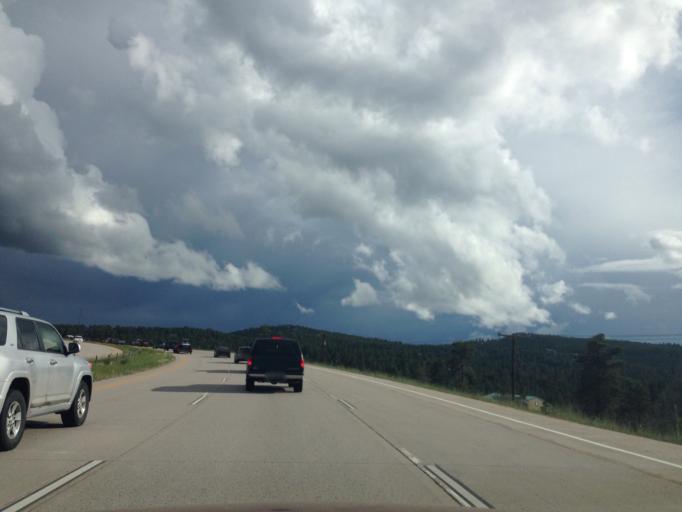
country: US
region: Colorado
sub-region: Jefferson County
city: Evergreen
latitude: 39.5286
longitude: -105.3074
